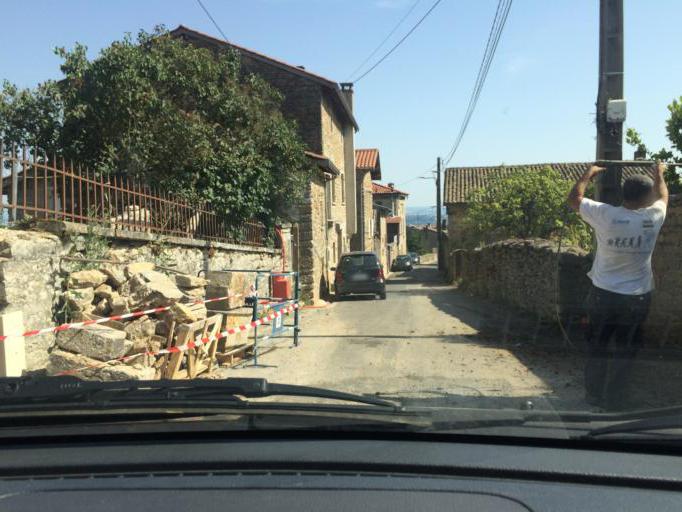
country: FR
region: Rhone-Alpes
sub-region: Departement du Rhone
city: Limonest
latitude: 45.8279
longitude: 4.7948
